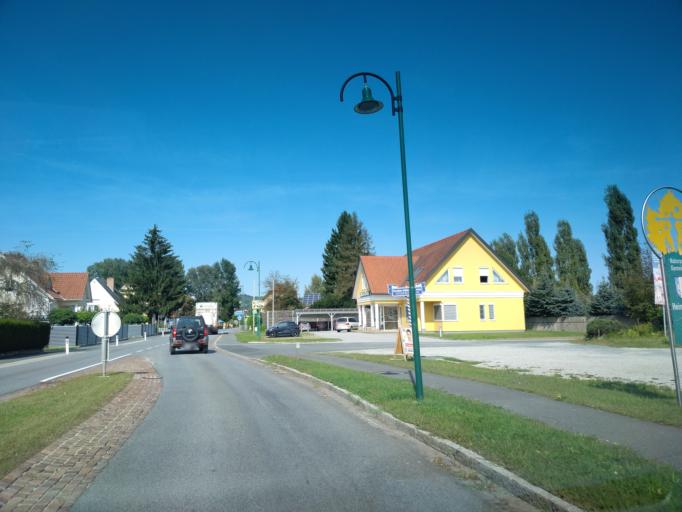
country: AT
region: Styria
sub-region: Politischer Bezirk Leibnitz
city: Heimschuh
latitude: 46.7586
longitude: 15.4877
